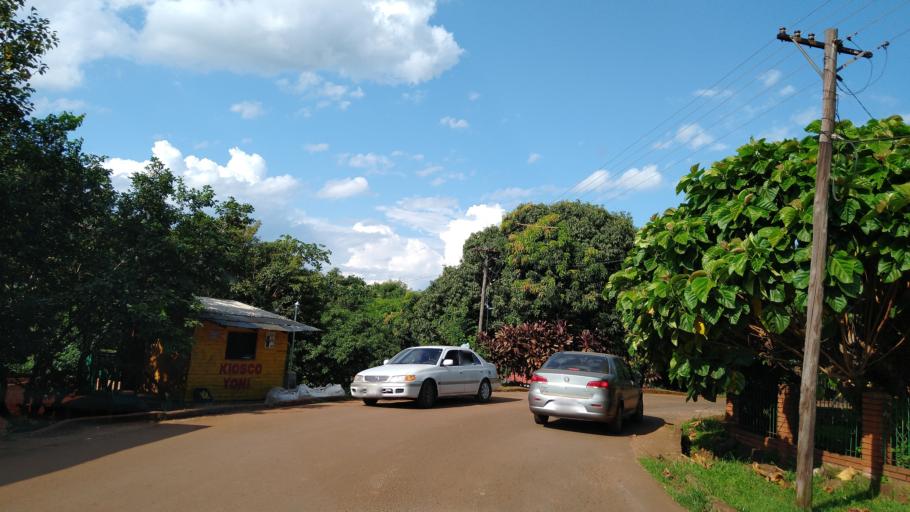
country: AR
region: Misiones
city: Puerto Piray
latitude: -26.4681
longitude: -54.7078
